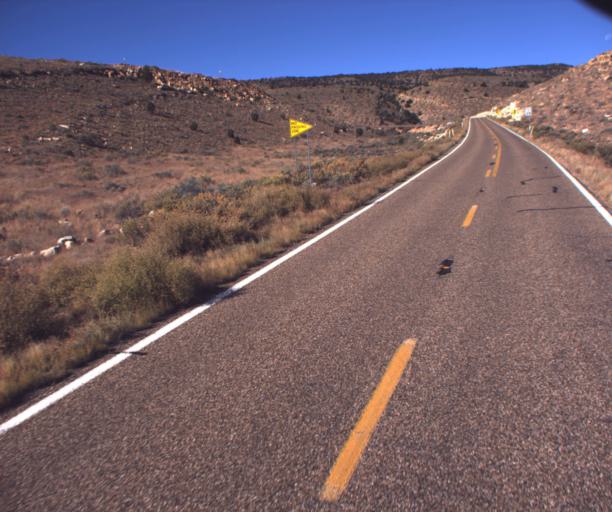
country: US
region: Arizona
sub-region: Coconino County
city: Fredonia
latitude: 36.7336
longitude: -112.0572
